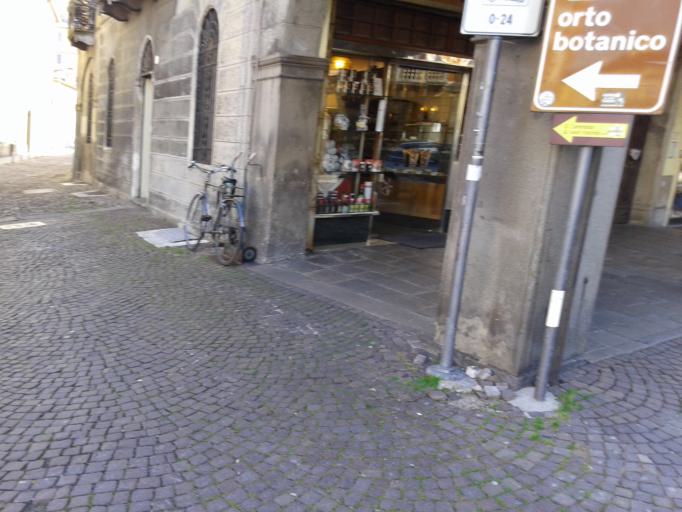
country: IT
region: Veneto
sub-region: Provincia di Padova
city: Padova
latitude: 45.4009
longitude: 11.8798
